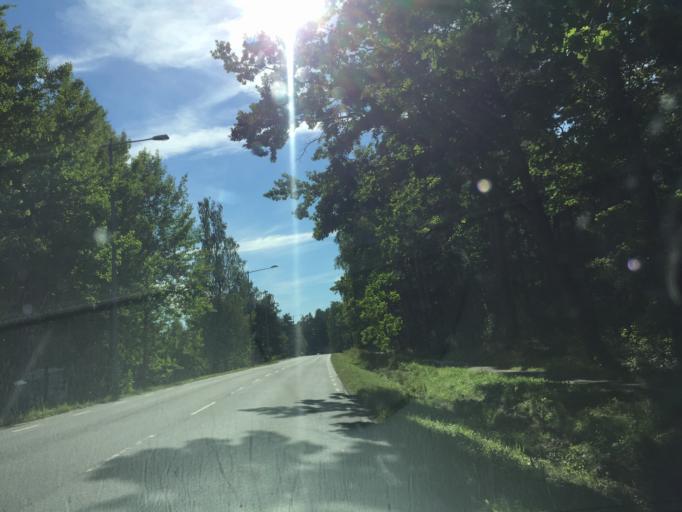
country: SE
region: OErebro
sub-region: Orebro Kommun
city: Orebro
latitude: 59.2962
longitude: 15.2514
